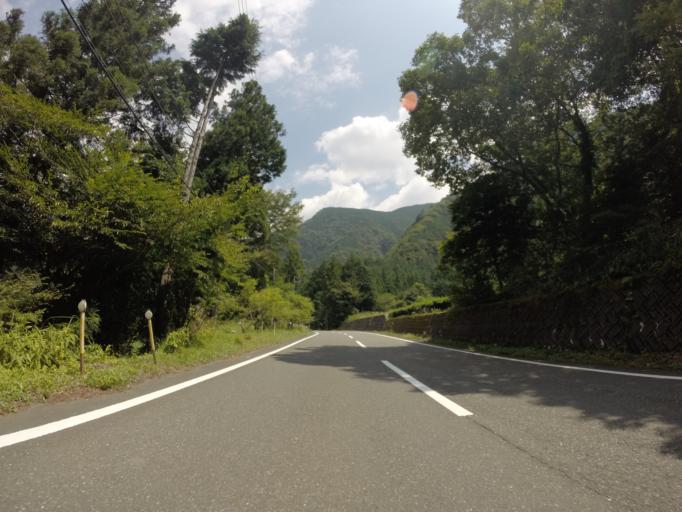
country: JP
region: Shizuoka
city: Shizuoka-shi
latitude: 35.2614
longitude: 138.3279
